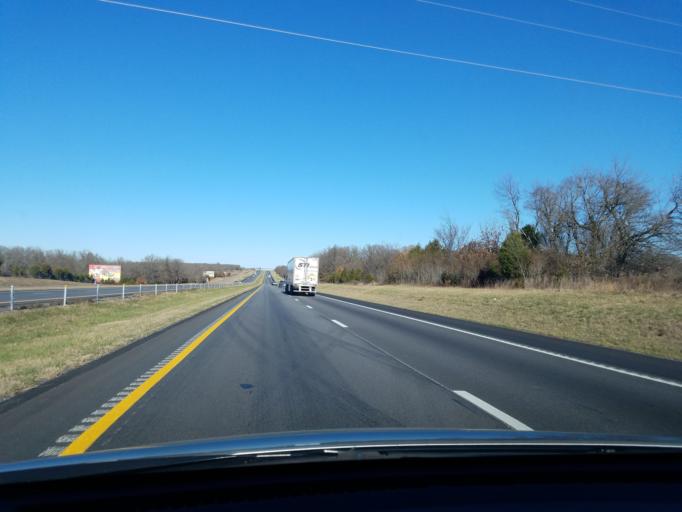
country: US
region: Missouri
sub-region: Webster County
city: Marshfield
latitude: 37.3684
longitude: -92.9071
